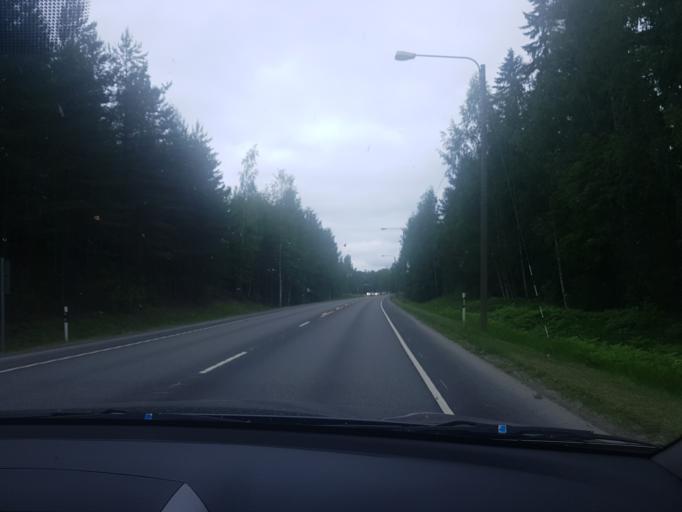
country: FI
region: Pirkanmaa
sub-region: Tampere
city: Kangasala
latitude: 61.4067
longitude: 24.1681
